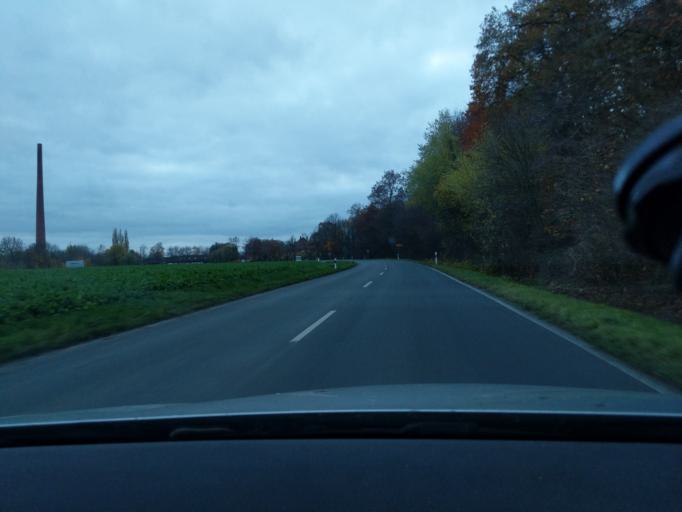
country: DE
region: North Rhine-Westphalia
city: Datteln
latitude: 51.6843
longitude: 7.4120
